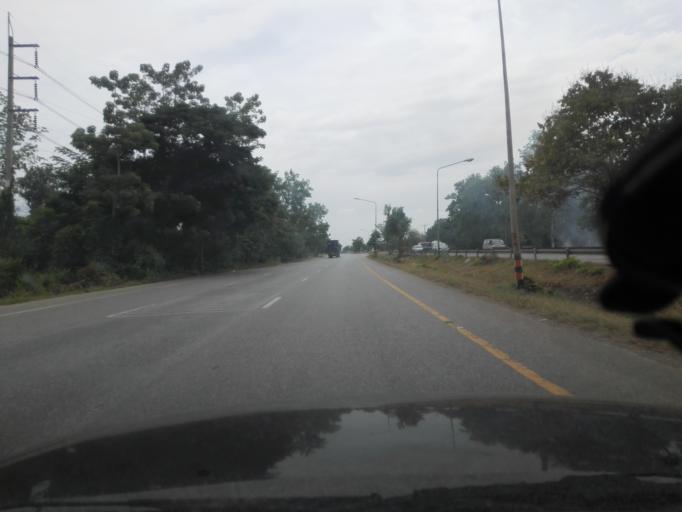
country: TH
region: Kamphaeng Phet
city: Khlong Khlung
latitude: 16.1069
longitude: 99.7189
